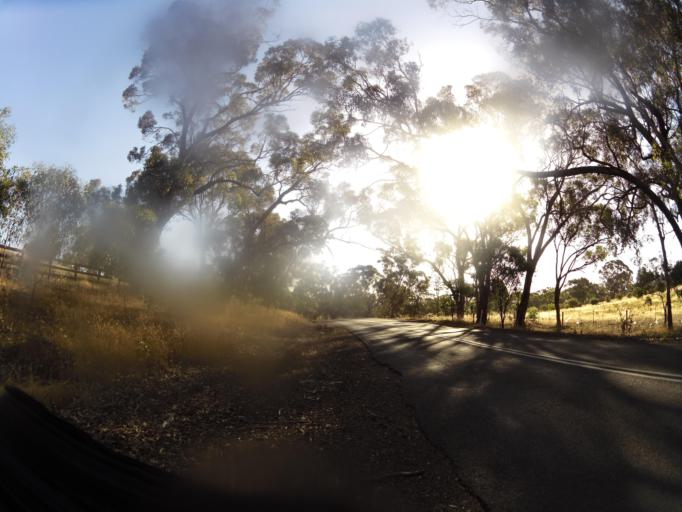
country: AU
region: Victoria
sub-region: Murrindindi
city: Kinglake West
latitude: -37.0116
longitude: 145.1199
